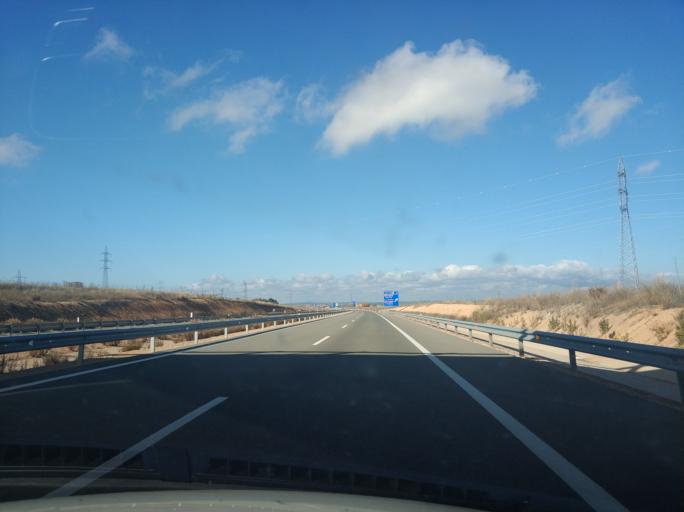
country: ES
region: Castille and Leon
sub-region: Provincia de Soria
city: Frechilla de Almazan
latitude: 41.4335
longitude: -2.4970
